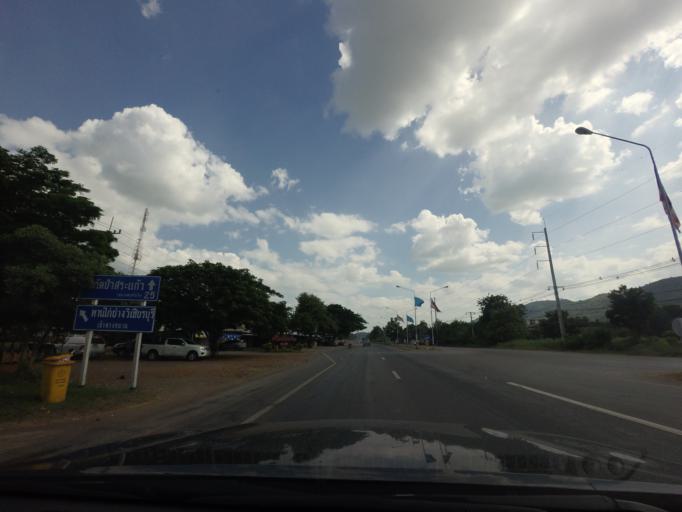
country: TH
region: Phetchabun
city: Wichian Buri
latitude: 15.6533
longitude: 101.0402
